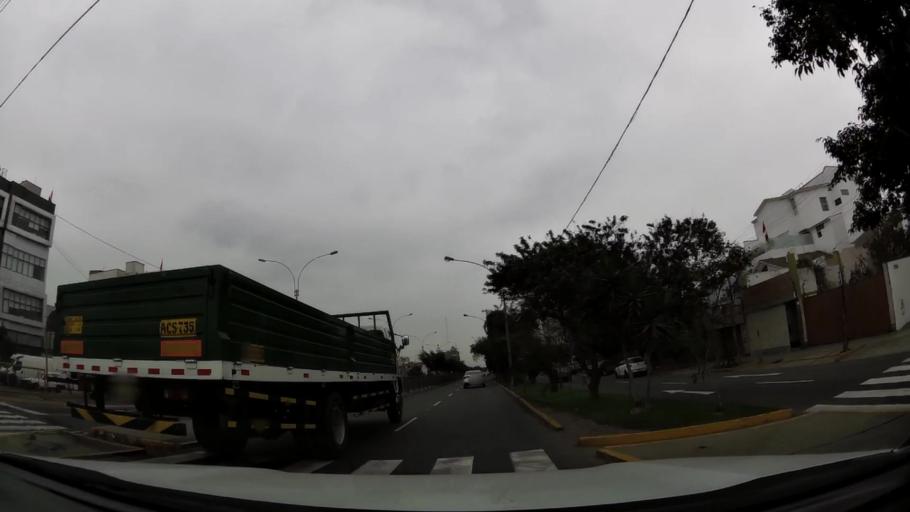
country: PE
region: Lima
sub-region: Lima
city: Surco
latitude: -12.1223
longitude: -77.0057
